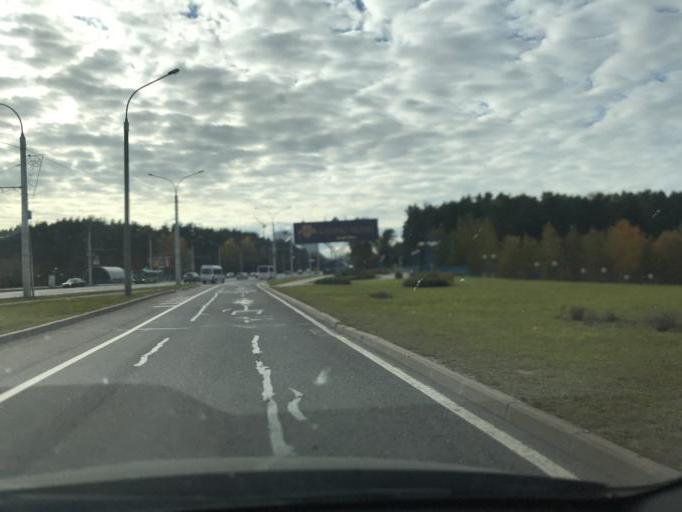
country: BY
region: Minsk
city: Borovlyany
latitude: 53.9396
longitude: 27.6682
